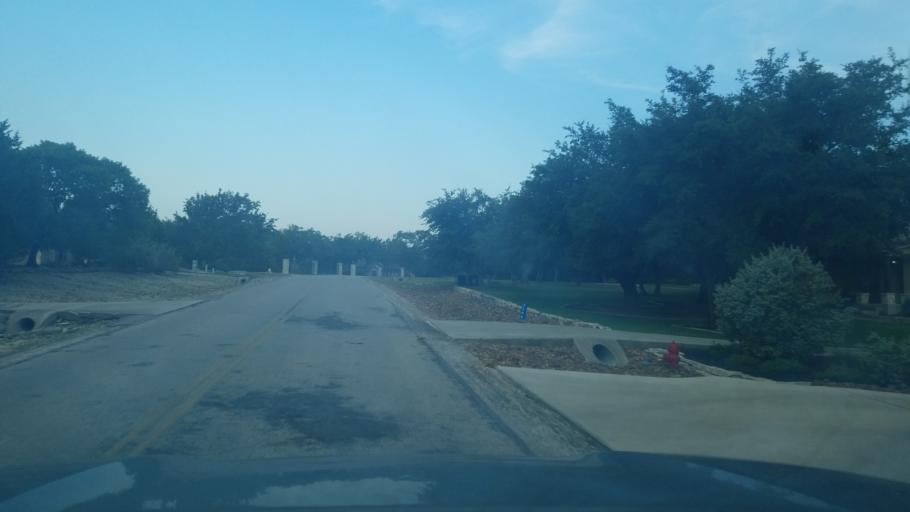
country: US
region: Texas
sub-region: Comal County
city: Bulverde
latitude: 29.8177
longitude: -98.4037
